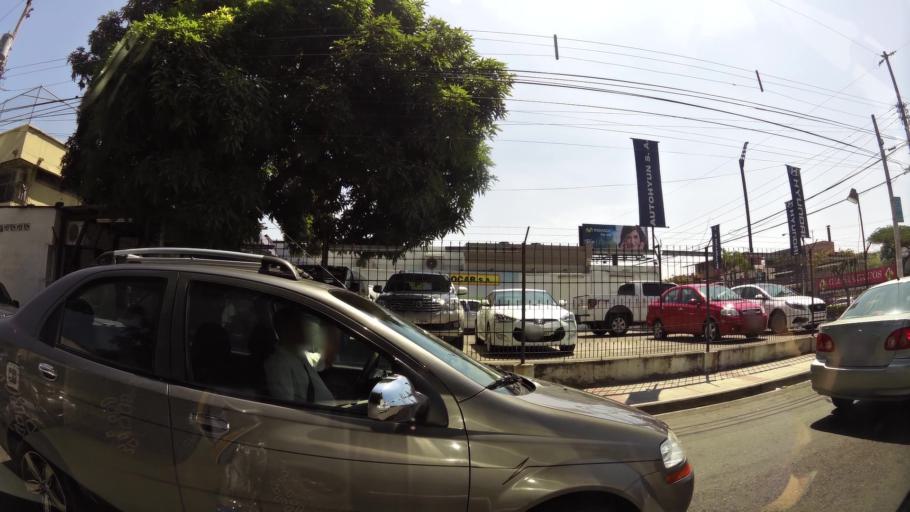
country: EC
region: Guayas
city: Guayaquil
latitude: -2.1646
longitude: -79.9125
